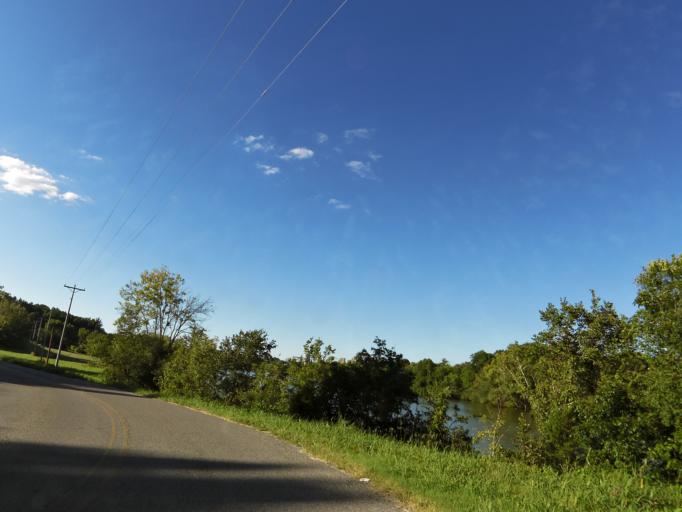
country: US
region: Tennessee
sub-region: Blount County
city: Eagleton Village
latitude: 35.8514
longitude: -83.9486
